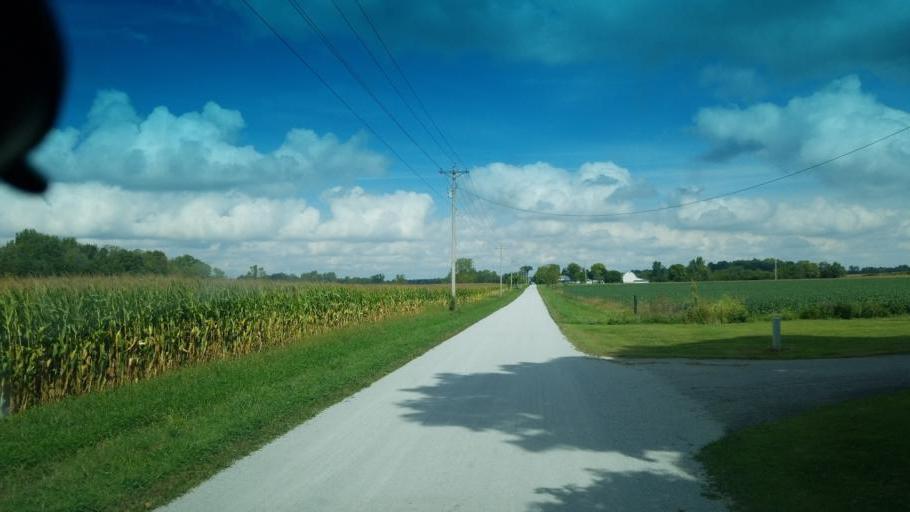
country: US
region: Ohio
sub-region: Seneca County
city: Tiffin
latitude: 40.9833
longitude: -83.1127
